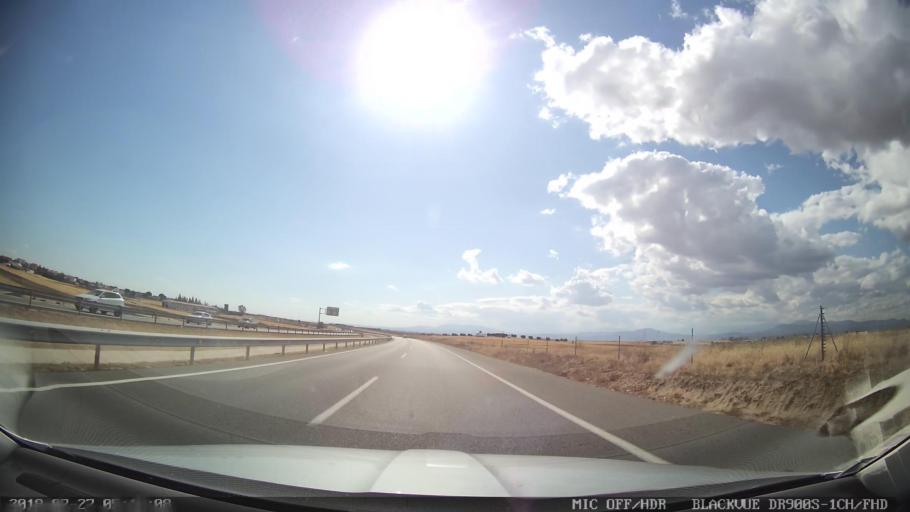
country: ES
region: Castille-La Mancha
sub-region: Province of Toledo
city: Quismondo
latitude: 40.1150
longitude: -4.3173
